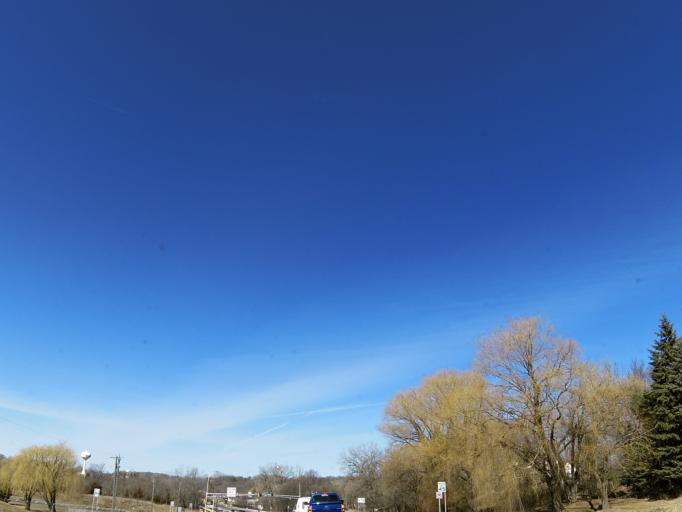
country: US
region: Minnesota
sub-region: Wright County
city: Rockford
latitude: 45.0840
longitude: -93.7310
